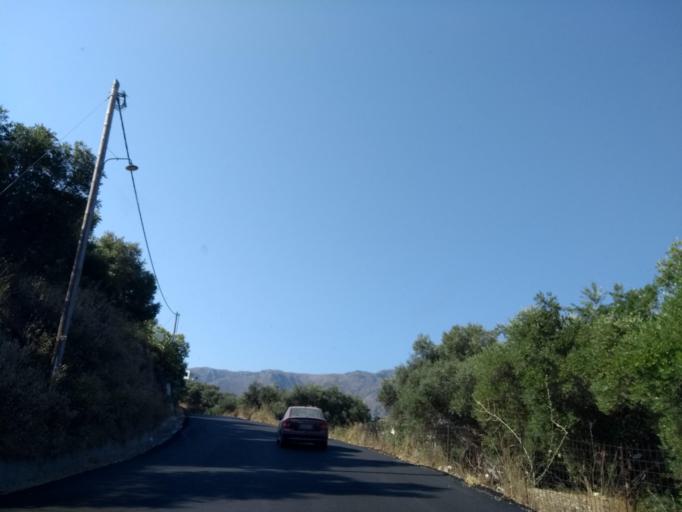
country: GR
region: Crete
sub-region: Nomos Chanias
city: Georgioupolis
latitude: 35.3255
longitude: 24.2997
